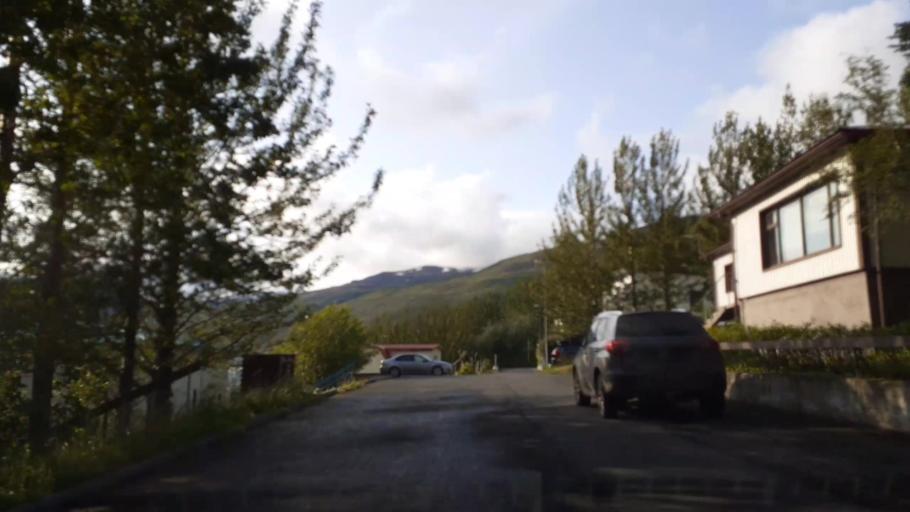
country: IS
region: East
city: Eskifjoerdur
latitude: 65.0673
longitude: -14.0039
